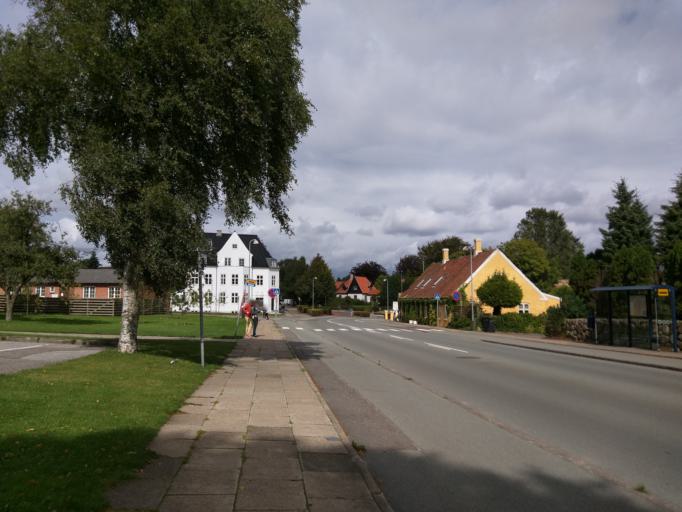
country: DK
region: Central Jutland
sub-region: Viborg Kommune
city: Viborg
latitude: 56.4577
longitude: 9.4081
